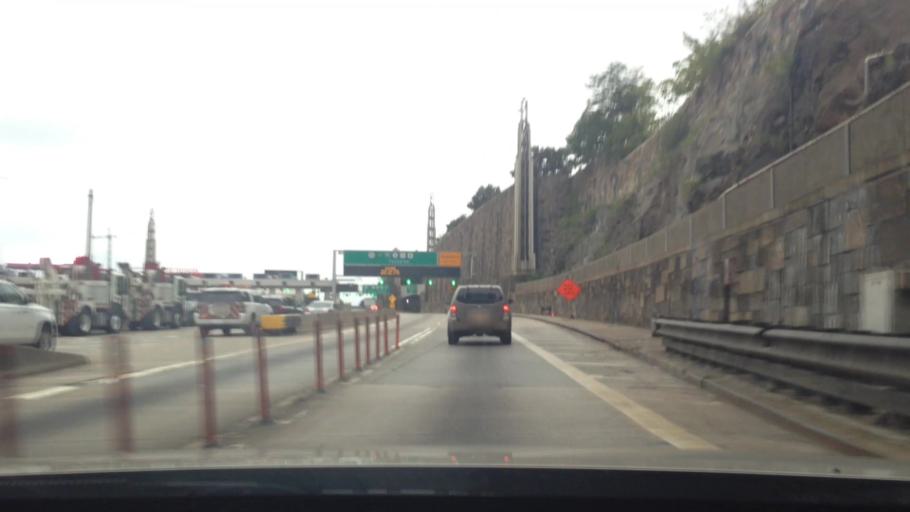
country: US
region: New Jersey
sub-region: Hudson County
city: Weehawken
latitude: 40.7663
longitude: -74.0230
